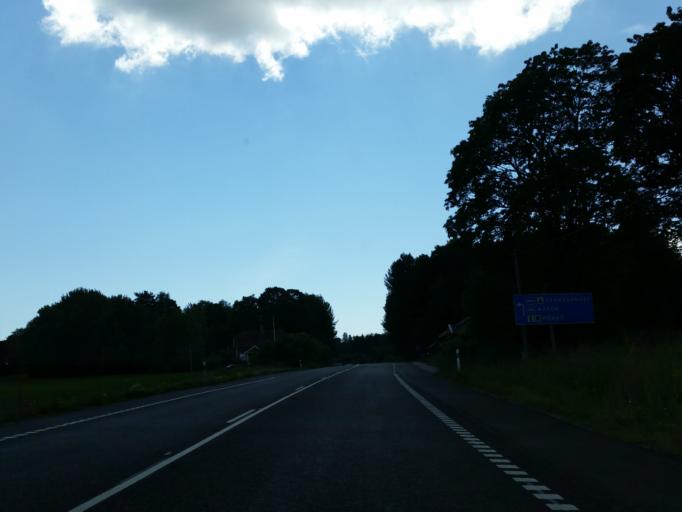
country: SE
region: Soedermanland
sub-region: Trosa Kommun
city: Vagnharad
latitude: 59.0078
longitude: 17.5966
